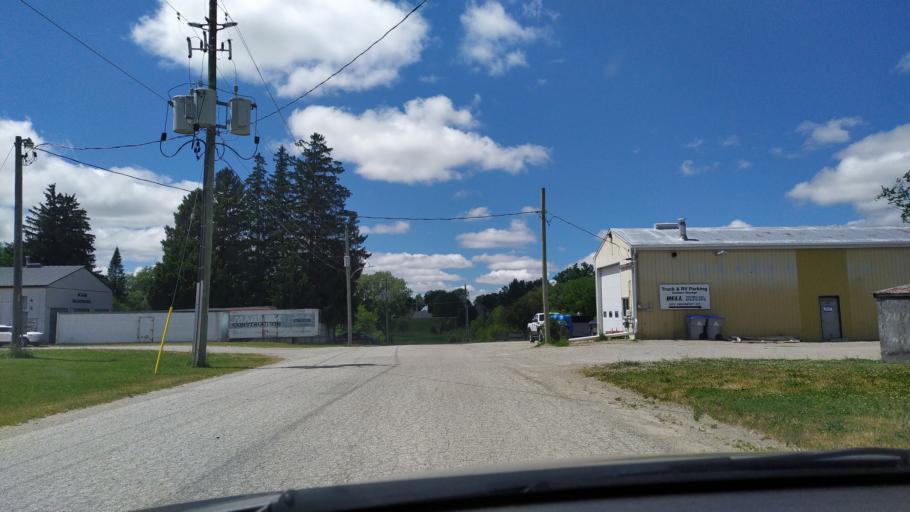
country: CA
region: Ontario
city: Huron East
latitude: 43.4611
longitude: -81.2001
